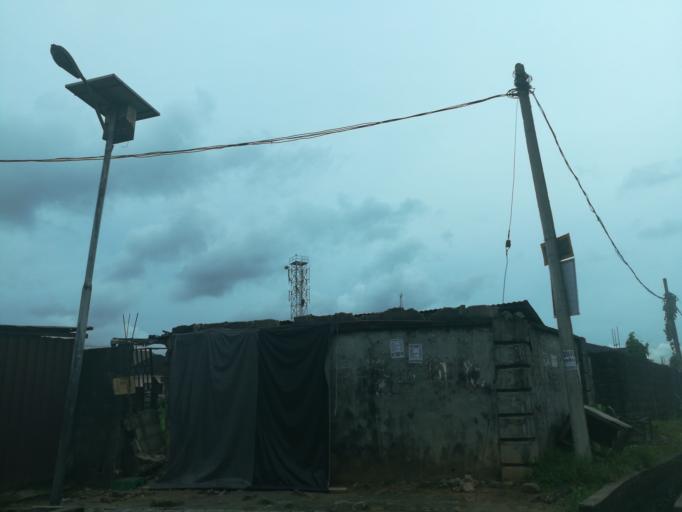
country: NG
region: Rivers
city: Port Harcourt
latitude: 4.8218
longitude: 6.9920
